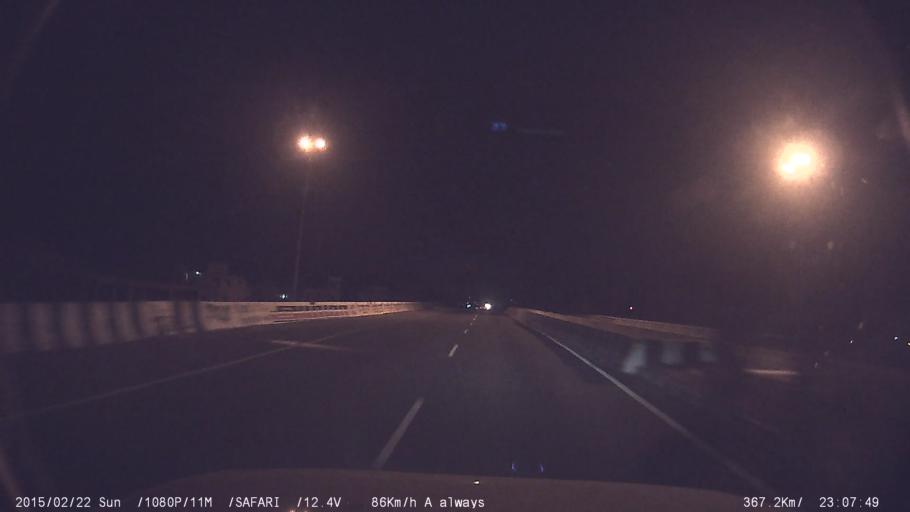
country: IN
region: Tamil Nadu
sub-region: Namakkal
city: Rasipuram
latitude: 11.4446
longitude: 78.1584
